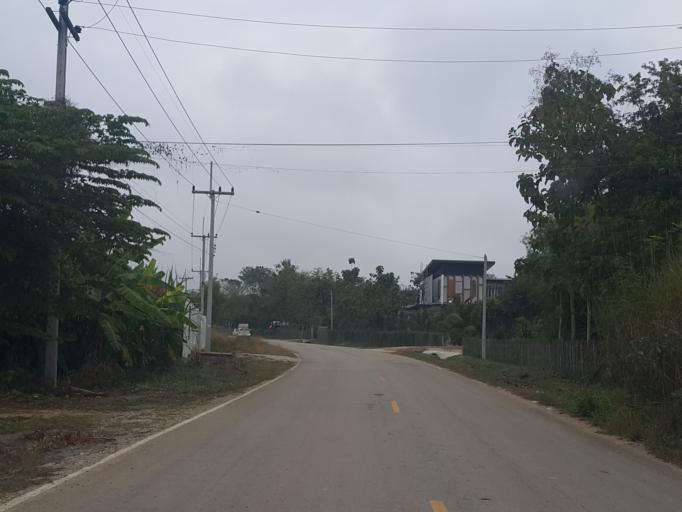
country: TH
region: Lampang
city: Lampang
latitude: 18.3311
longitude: 99.4865
